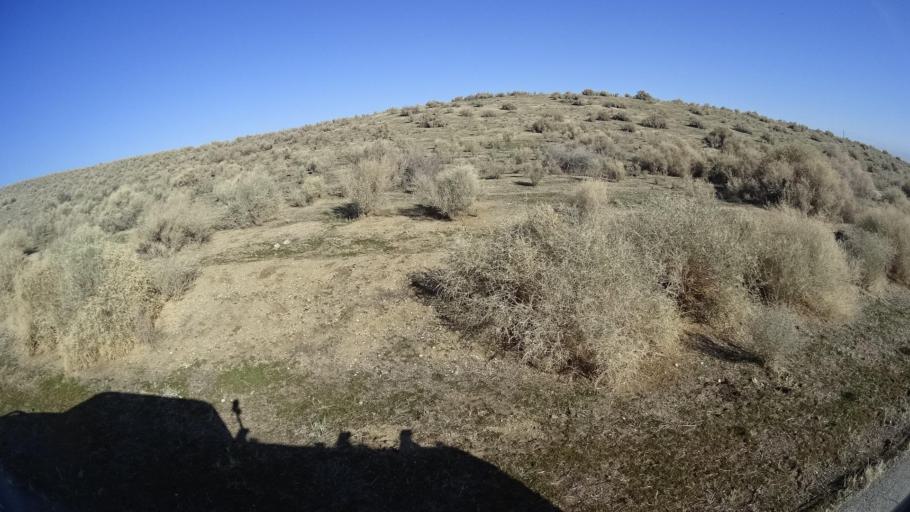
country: US
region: California
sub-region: Kern County
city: Taft Heights
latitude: 35.2281
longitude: -119.6388
